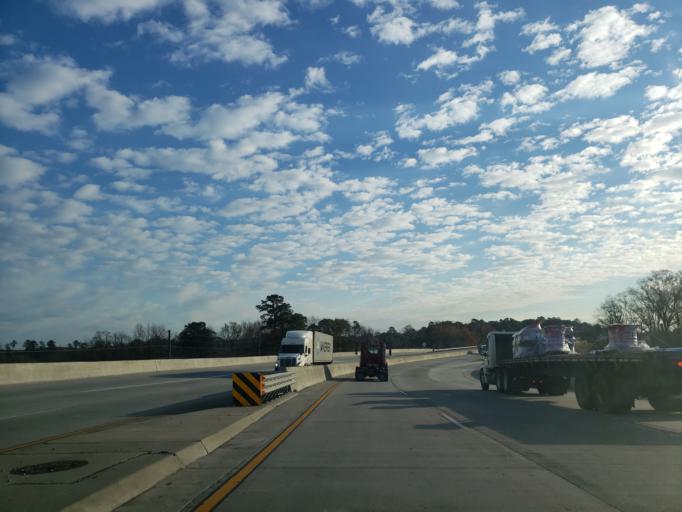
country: US
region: Georgia
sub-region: Chatham County
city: Port Wentworth
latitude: 32.1636
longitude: -81.1830
